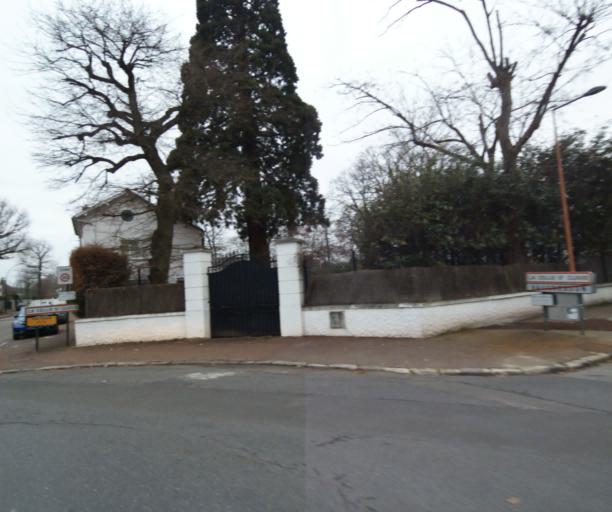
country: FR
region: Ile-de-France
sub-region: Departement des Yvelines
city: La Celle-Saint-Cloud
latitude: 48.8469
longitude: 2.1504
